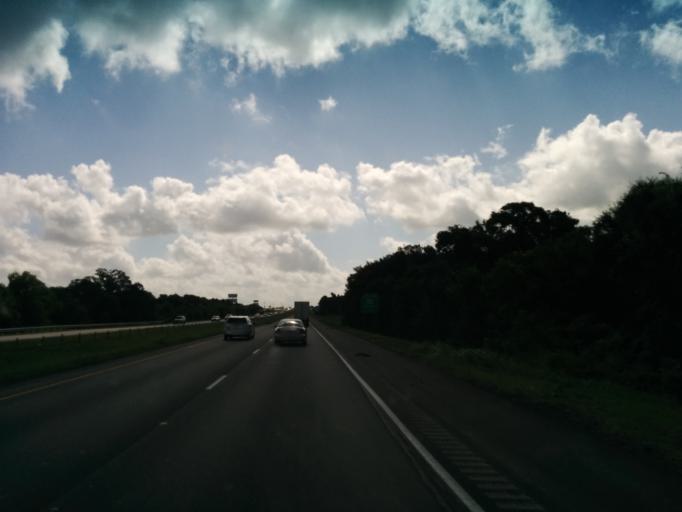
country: US
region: Texas
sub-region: Colorado County
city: Weimar
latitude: 29.6902
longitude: -96.7965
